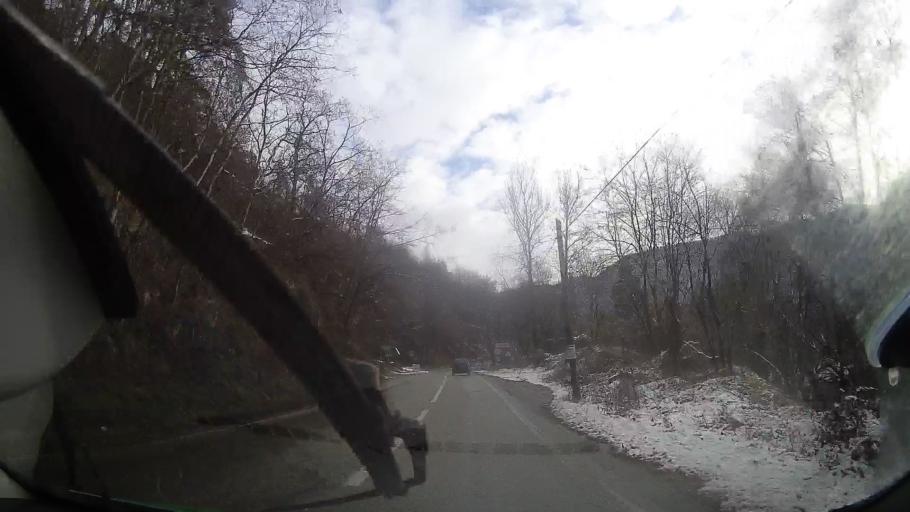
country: RO
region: Alba
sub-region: Oras Baia de Aries
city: Baia de Aries
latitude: 46.4019
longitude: 23.3063
